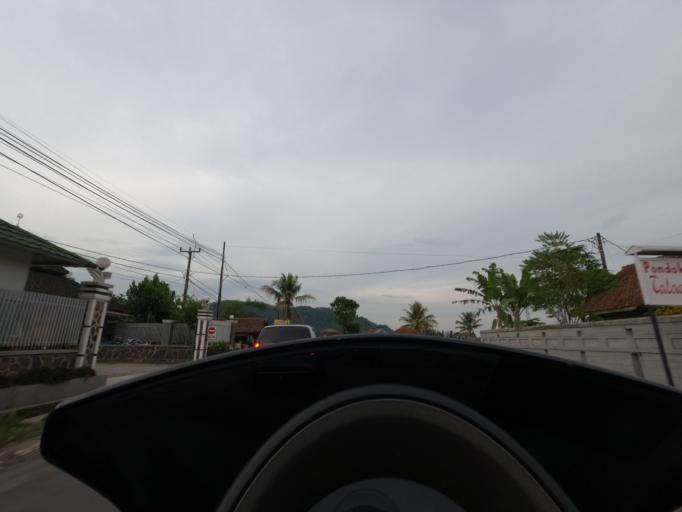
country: ID
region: West Java
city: Lembang
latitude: -6.6588
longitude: 107.7129
